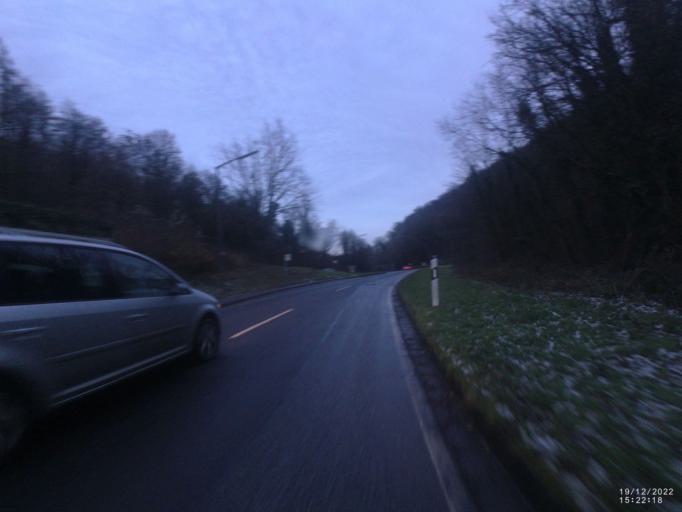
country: DE
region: Rheinland-Pfalz
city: Unkel
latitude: 50.5994
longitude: 7.2029
